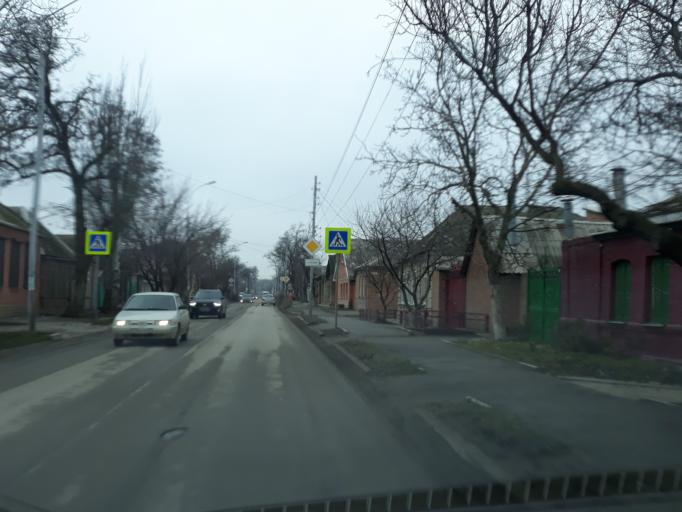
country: RU
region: Rostov
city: Taganrog
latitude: 47.2297
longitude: 38.9244
